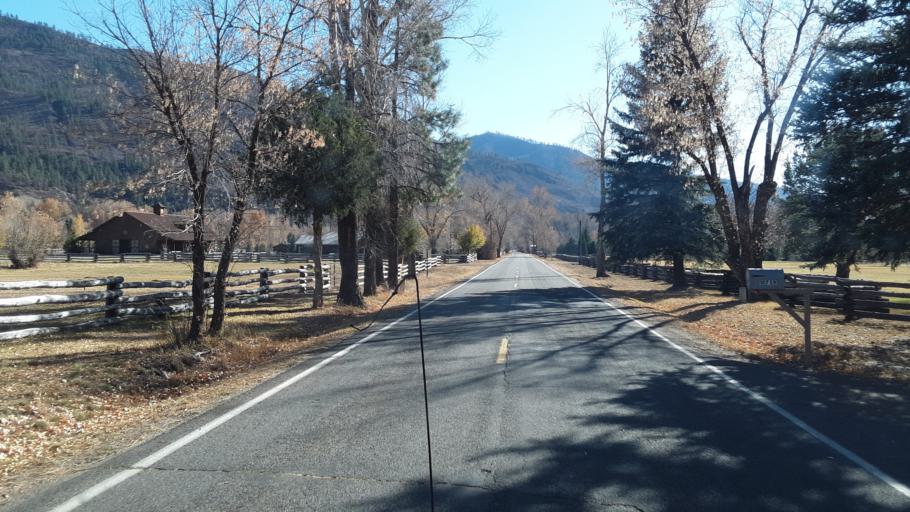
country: US
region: Colorado
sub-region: La Plata County
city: Durango
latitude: 37.4341
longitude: -107.7996
